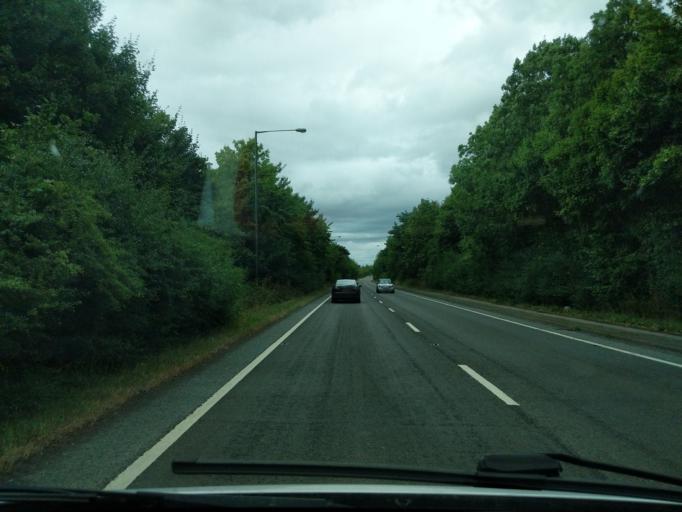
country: GB
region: England
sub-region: Cheshire West and Chester
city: Cuddington
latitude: 53.2516
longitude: -2.5936
